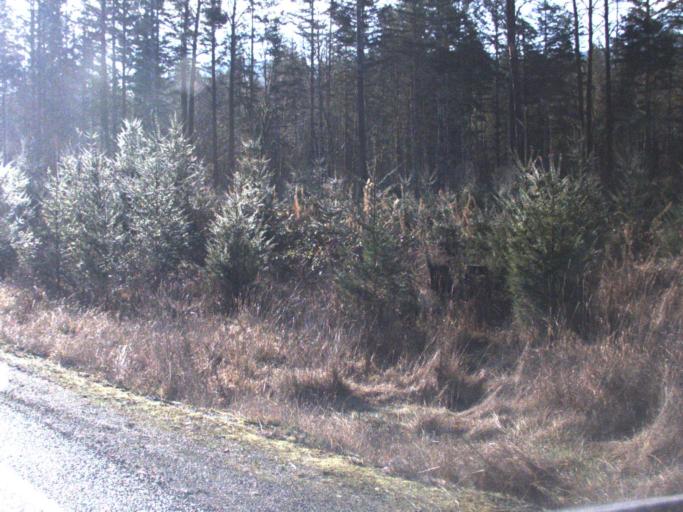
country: US
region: Washington
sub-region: Snohomish County
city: Darrington
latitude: 48.4747
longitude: -121.5899
